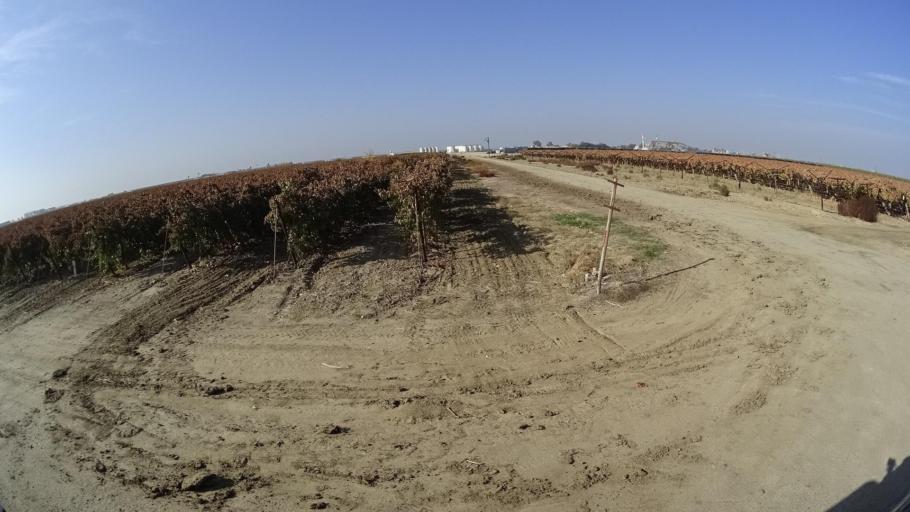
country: US
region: California
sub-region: Kern County
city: McFarland
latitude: 35.7142
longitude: -119.2232
